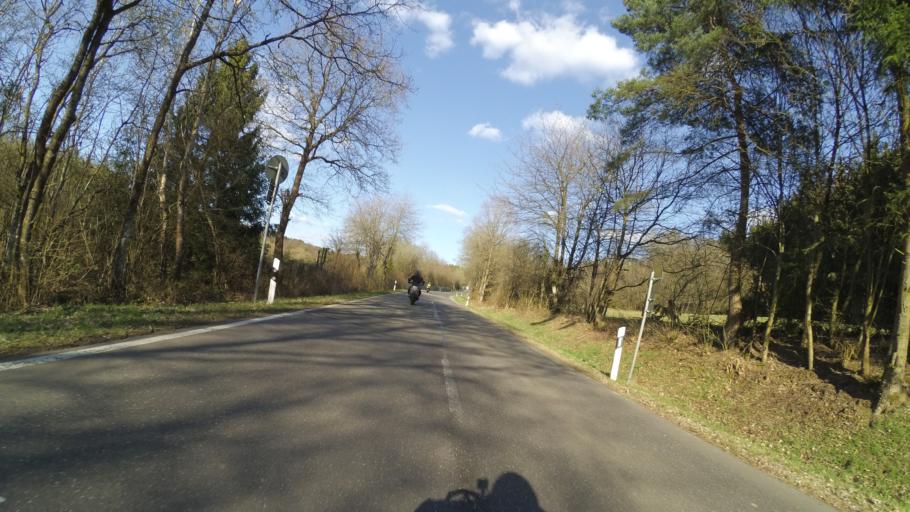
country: DE
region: Rheinland-Pfalz
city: Mullenbach
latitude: 50.3192
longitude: 6.9339
